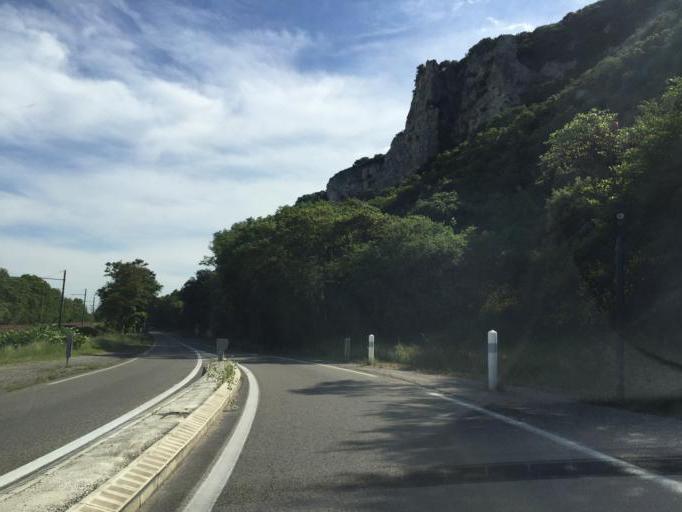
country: FR
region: Rhone-Alpes
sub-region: Departement de l'Ardeche
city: Cruas
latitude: 44.6325
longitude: 4.7442
